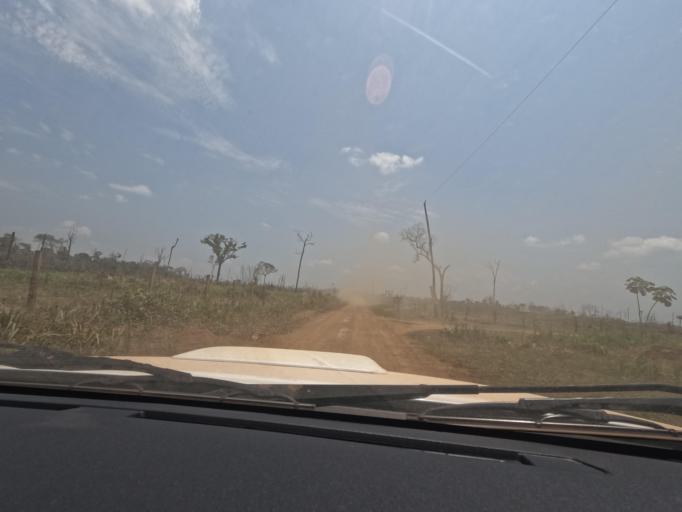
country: BR
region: Rondonia
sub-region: Porto Velho
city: Porto Velho
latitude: -8.6460
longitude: -64.1750
